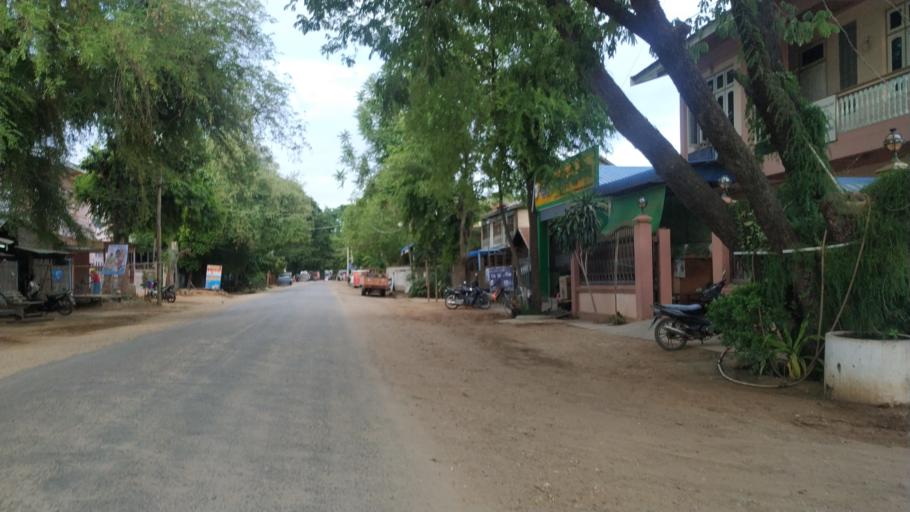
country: MM
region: Magway
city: Pakokku
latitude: 21.3356
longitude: 95.0740
